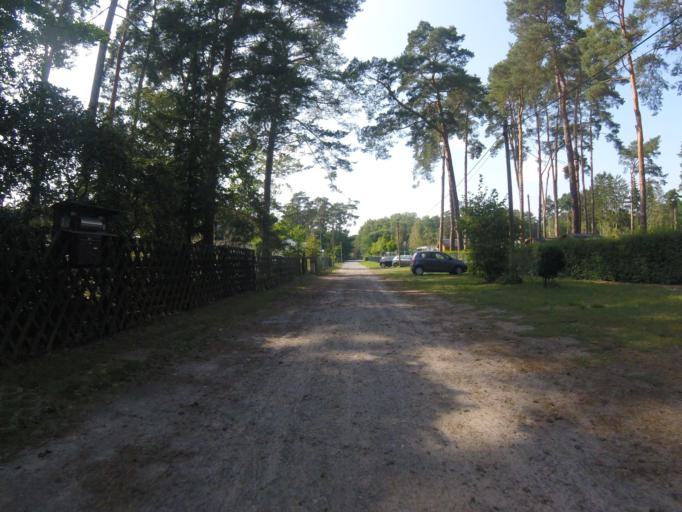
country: DE
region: Brandenburg
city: Bestensee
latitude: 52.2698
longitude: 13.7453
